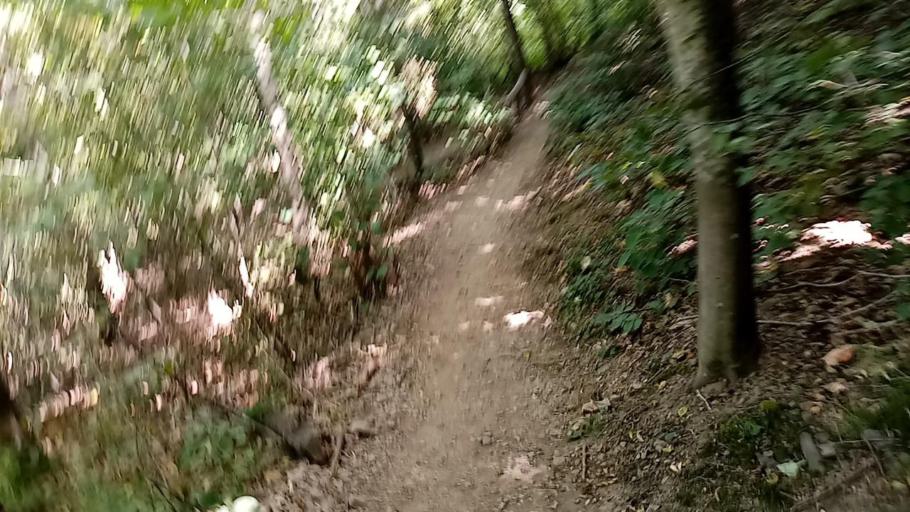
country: FR
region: Rhone-Alpes
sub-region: Departement du Rhone
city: Grandris
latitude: 46.0082
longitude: 4.5438
